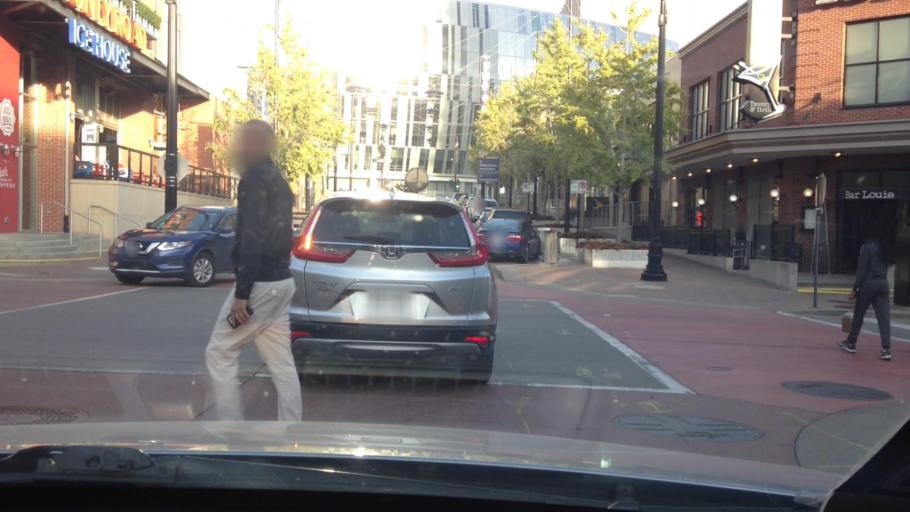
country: US
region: Missouri
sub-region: Jackson County
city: Kansas City
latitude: 39.0972
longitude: -94.5824
